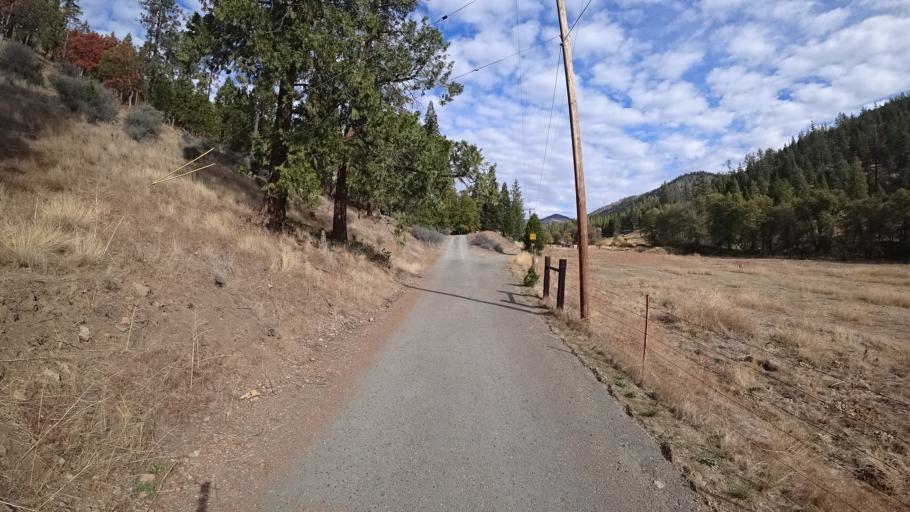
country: US
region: California
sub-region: Siskiyou County
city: Yreka
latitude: 41.6420
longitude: -122.7509
